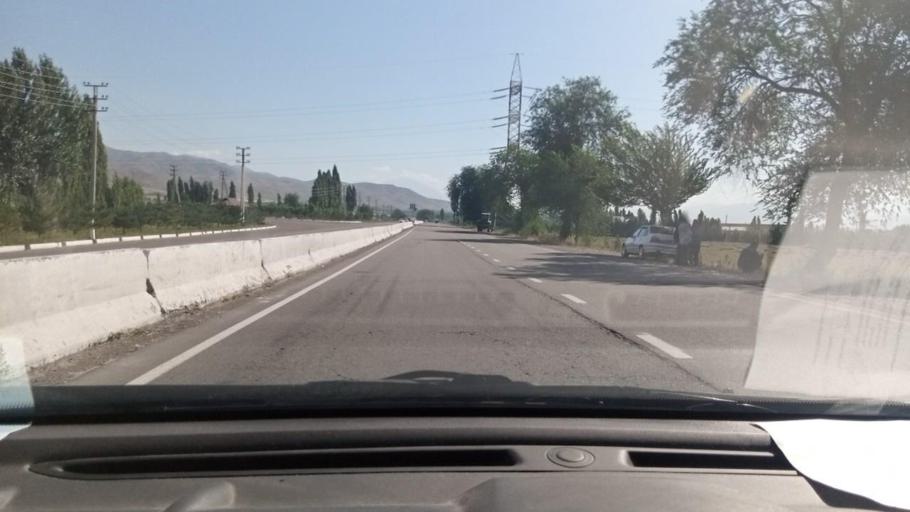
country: UZ
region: Toshkent
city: Ohangaron
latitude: 40.9159
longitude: 69.8293
